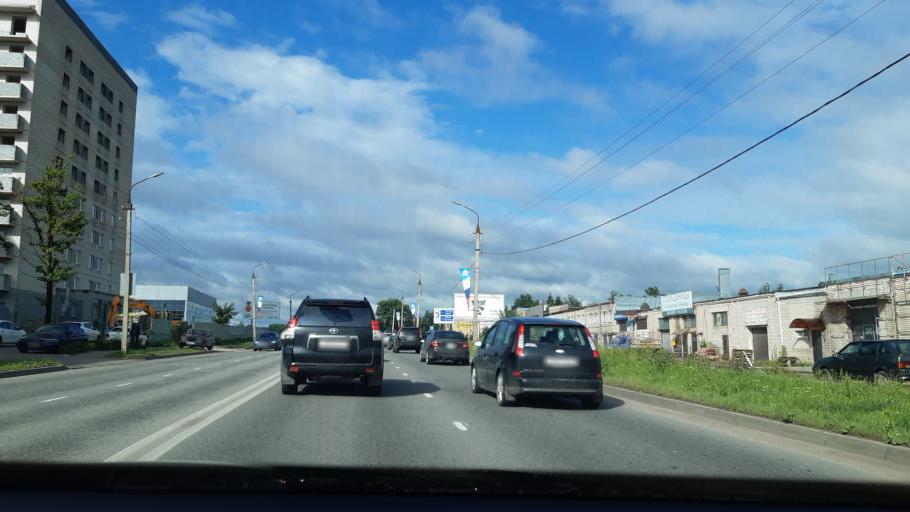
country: RU
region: Smolensk
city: Smolensk
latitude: 54.7579
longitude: 32.0761
